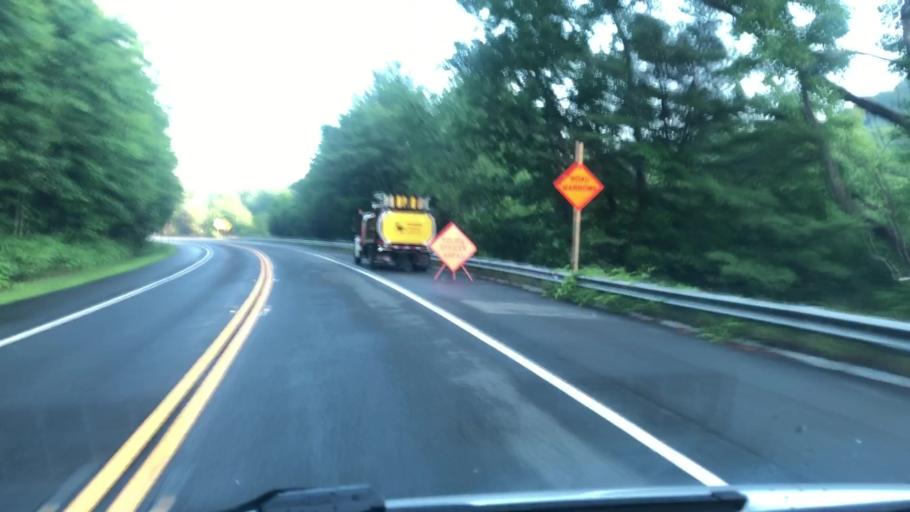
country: US
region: Massachusetts
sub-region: Hampshire County
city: Chesterfield
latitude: 42.4907
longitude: -72.9697
